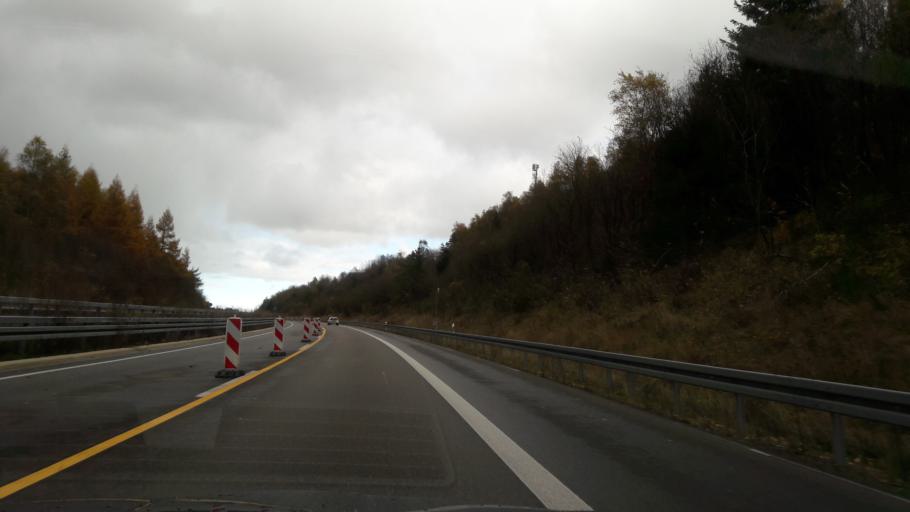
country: DE
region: Rheinland-Pfalz
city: Neuhutten
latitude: 49.5895
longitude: 7.0214
